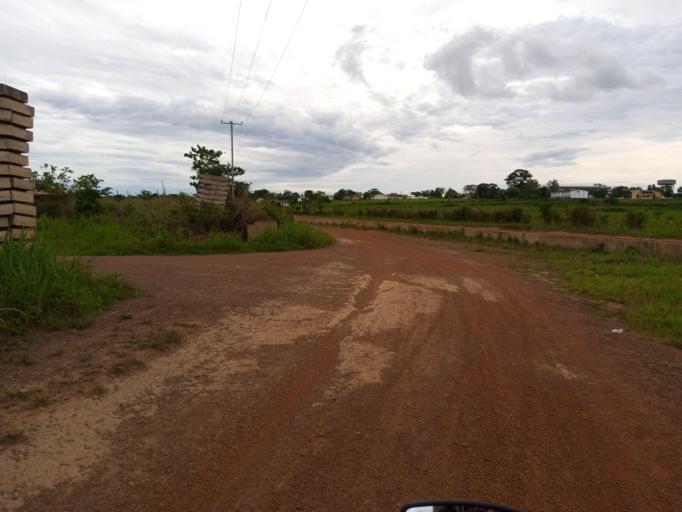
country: SL
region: Southern Province
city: Largo
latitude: 8.1146
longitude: -12.0630
